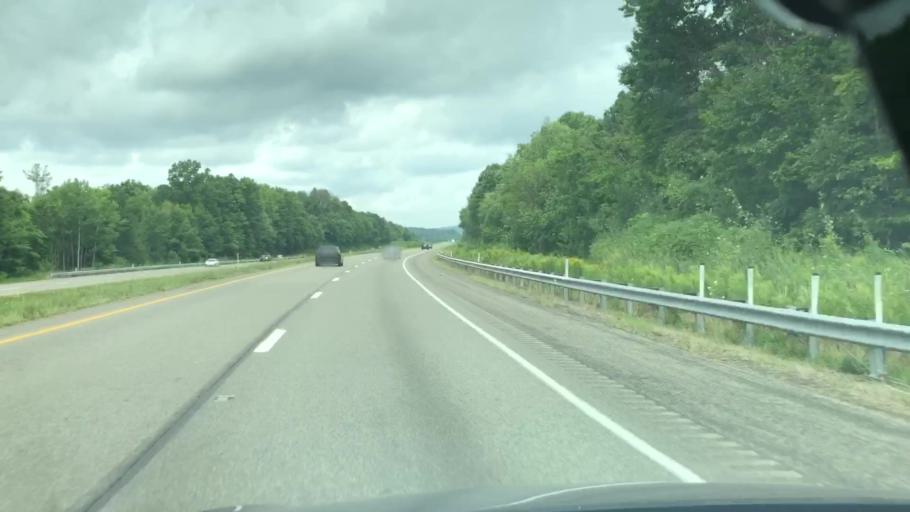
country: US
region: Pennsylvania
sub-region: Crawford County
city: Meadville
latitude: 41.5727
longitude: -80.1817
